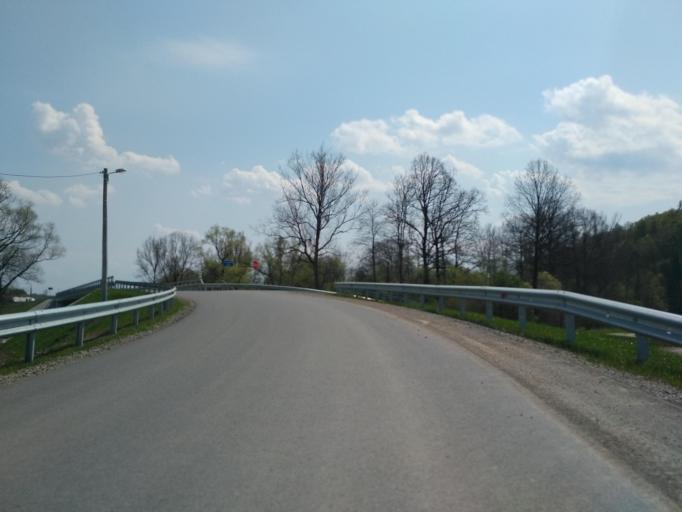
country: PL
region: Subcarpathian Voivodeship
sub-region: Powiat krosnienski
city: Jedlicze
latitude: 49.7282
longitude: 21.6209
